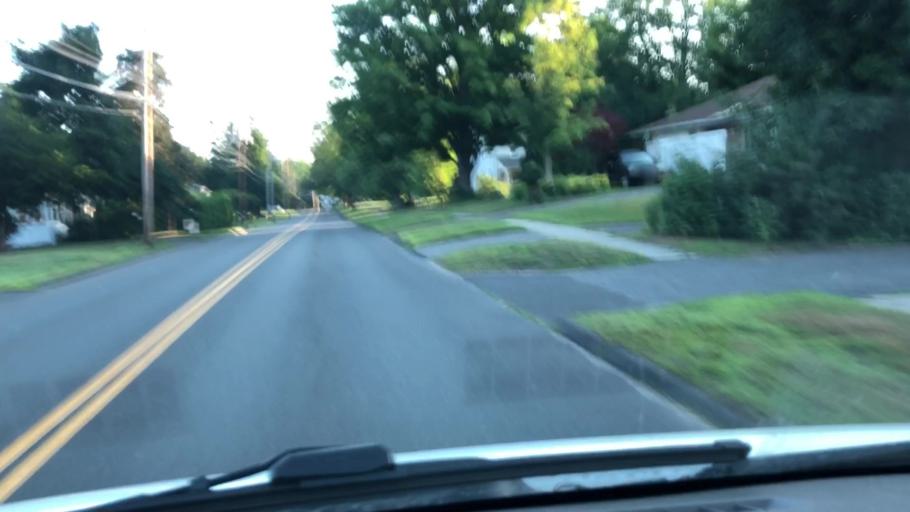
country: US
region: Massachusetts
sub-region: Hampshire County
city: Easthampton
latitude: 42.2562
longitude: -72.6789
